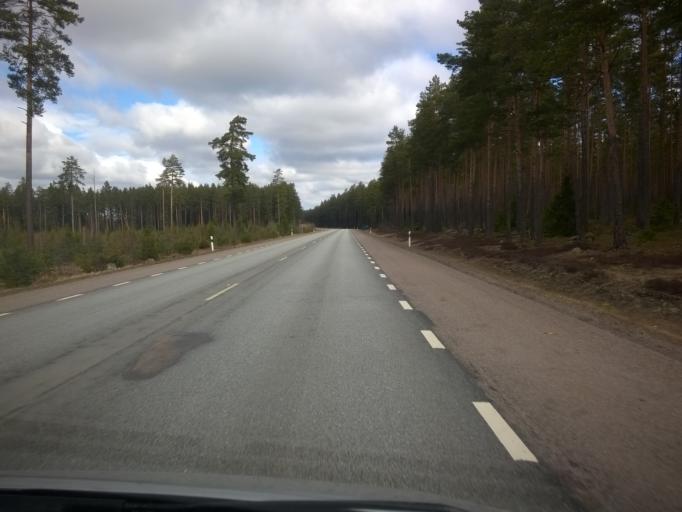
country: SE
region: Uppsala
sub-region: Tierps Kommun
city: Tierp
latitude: 60.1965
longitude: 17.4804
